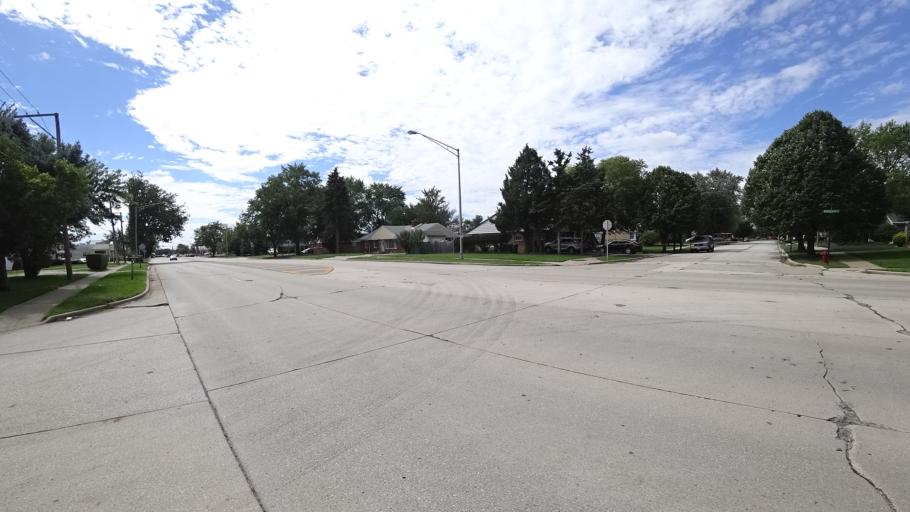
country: US
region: Illinois
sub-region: Cook County
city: Burbank
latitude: 41.7223
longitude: -87.7799
